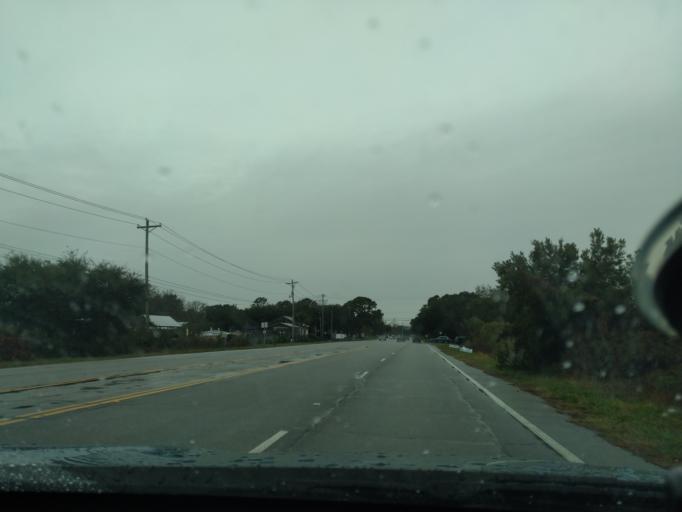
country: US
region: South Carolina
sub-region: Charleston County
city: Folly Beach
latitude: 32.6908
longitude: -79.9632
